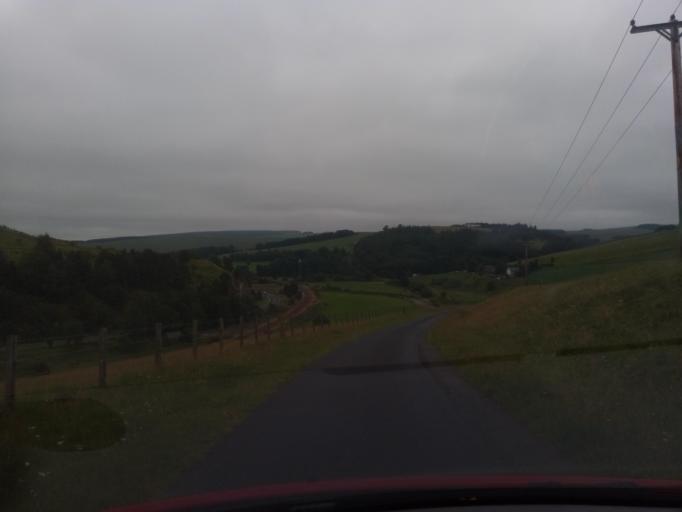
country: GB
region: Scotland
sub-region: Fife
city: Pathhead
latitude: 55.7488
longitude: -2.9203
